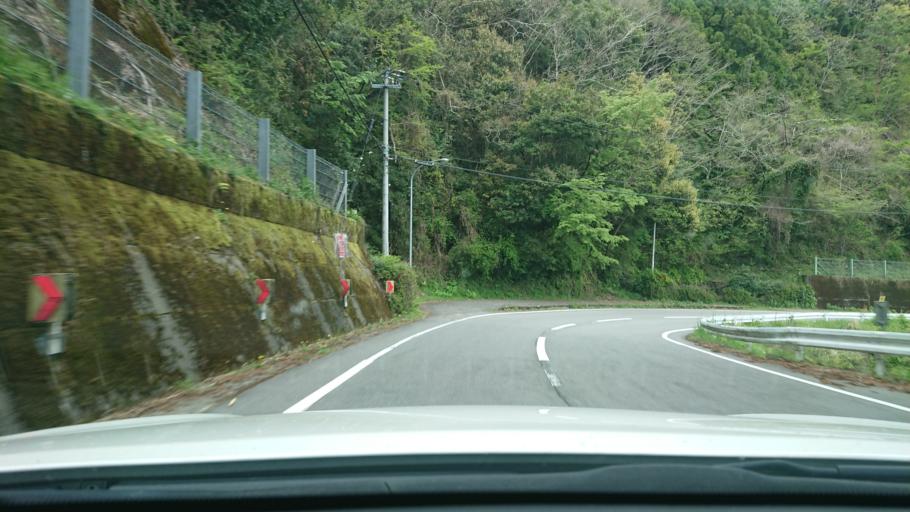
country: JP
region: Tokushima
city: Ishii
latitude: 33.9074
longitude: 134.4201
